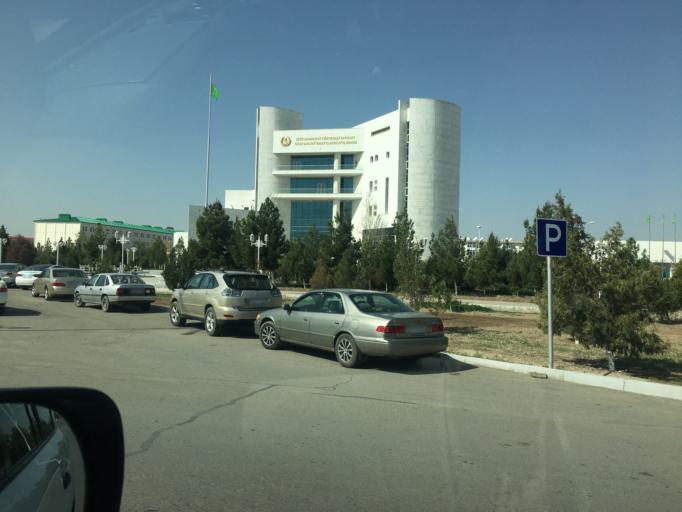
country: TM
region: Lebap
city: Turkmenabat
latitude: 39.0434
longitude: 63.5884
